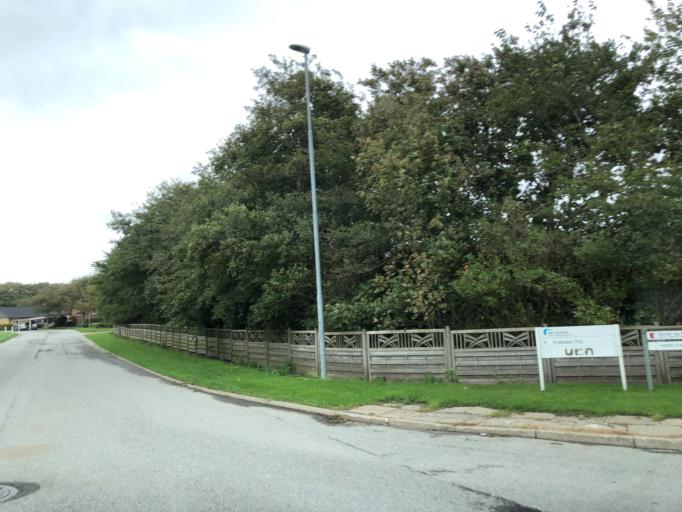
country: DK
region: North Denmark
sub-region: Thisted Kommune
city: Thisted
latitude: 56.9664
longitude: 8.6892
